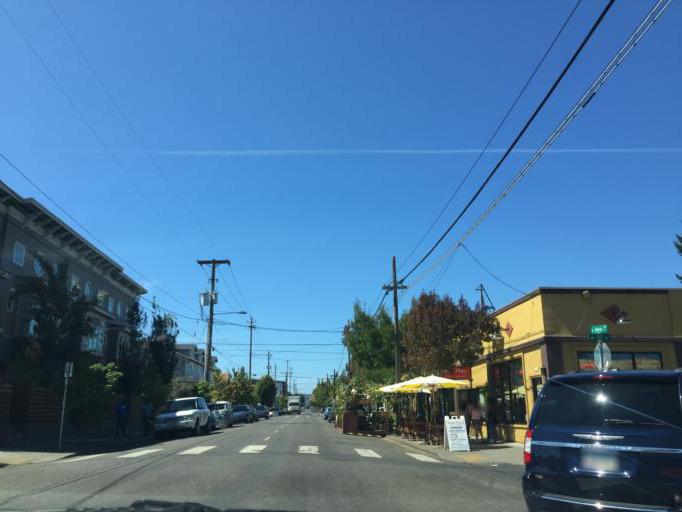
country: US
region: Oregon
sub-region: Multnomah County
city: Portland
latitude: 45.5591
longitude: -122.6387
